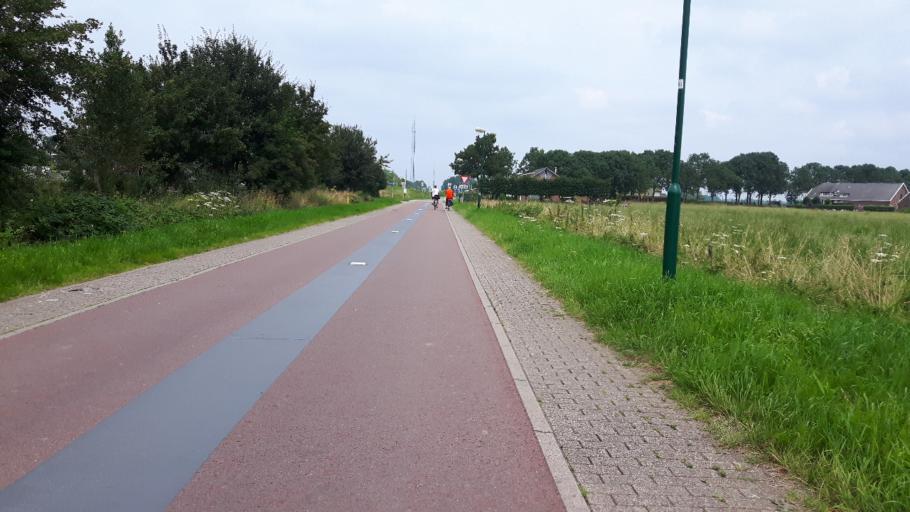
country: NL
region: Utrecht
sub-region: Gemeente Houten
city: Houten
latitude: 52.0313
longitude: 5.1845
